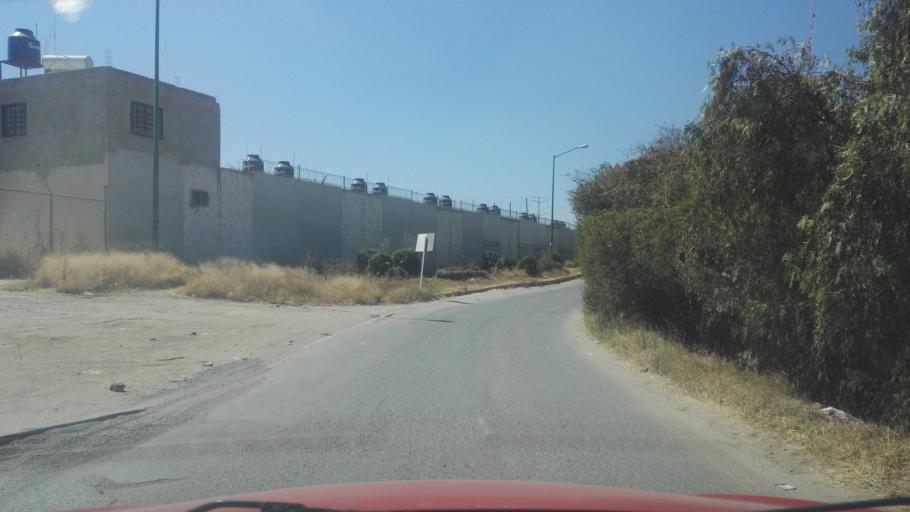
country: MX
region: Guanajuato
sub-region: Leon
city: Fraccionamiento Paraiso Real
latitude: 21.0841
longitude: -101.5932
